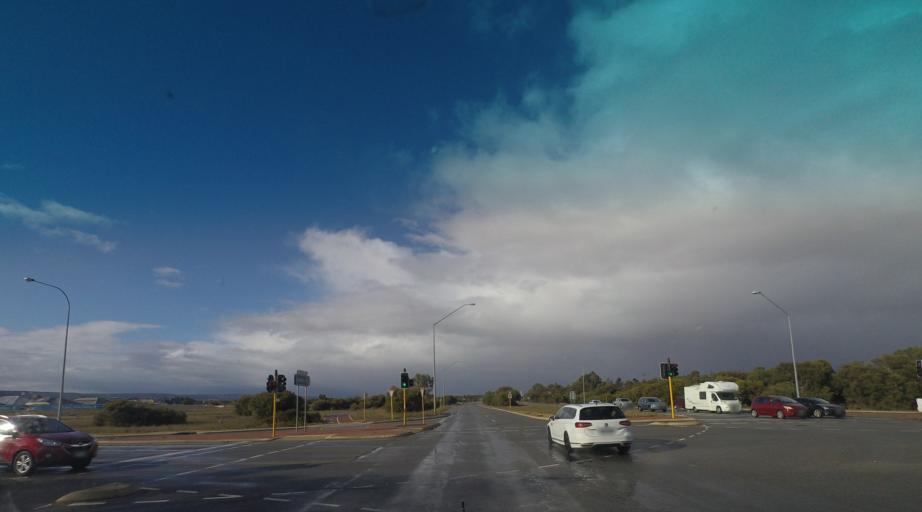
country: AU
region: Western Australia
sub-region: Serpentine-Jarrahdale
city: Oakford
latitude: -32.1797
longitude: 115.9621
